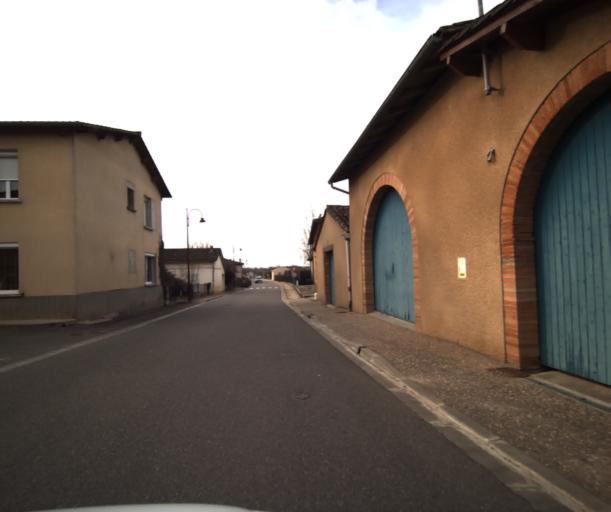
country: FR
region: Midi-Pyrenees
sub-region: Departement du Tarn-et-Garonne
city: Campsas
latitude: 43.8979
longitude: 1.3242
